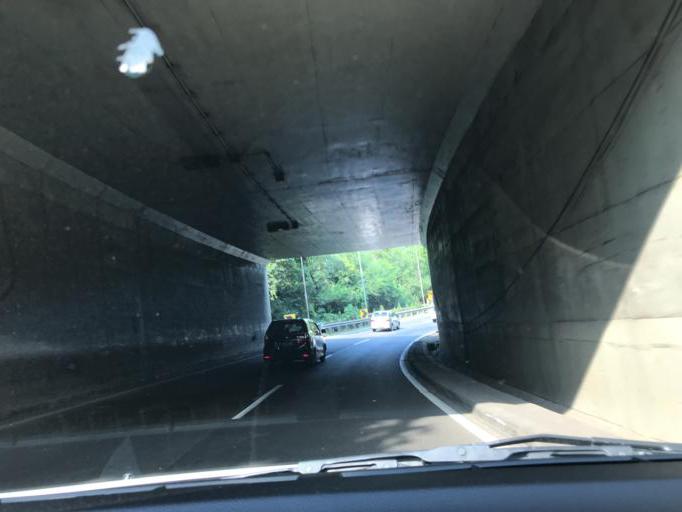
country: ID
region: Jakarta Raya
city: Jakarta
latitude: -6.2458
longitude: 106.8770
